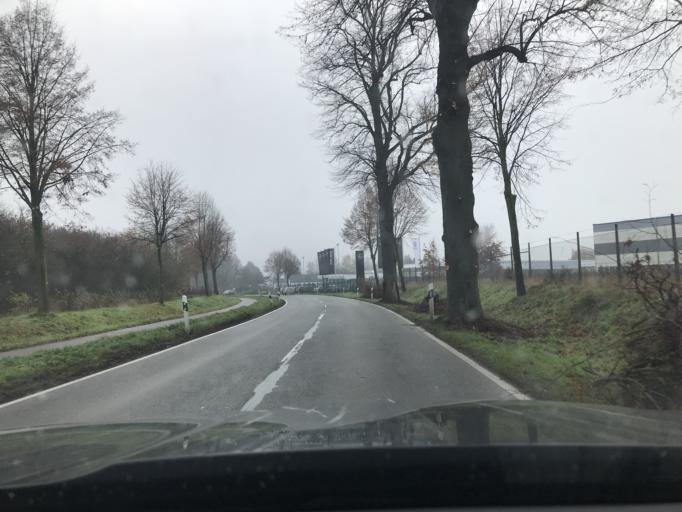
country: DE
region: North Rhine-Westphalia
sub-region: Regierungsbezirk Dusseldorf
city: Nettetal
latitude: 51.2889
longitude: 6.2606
